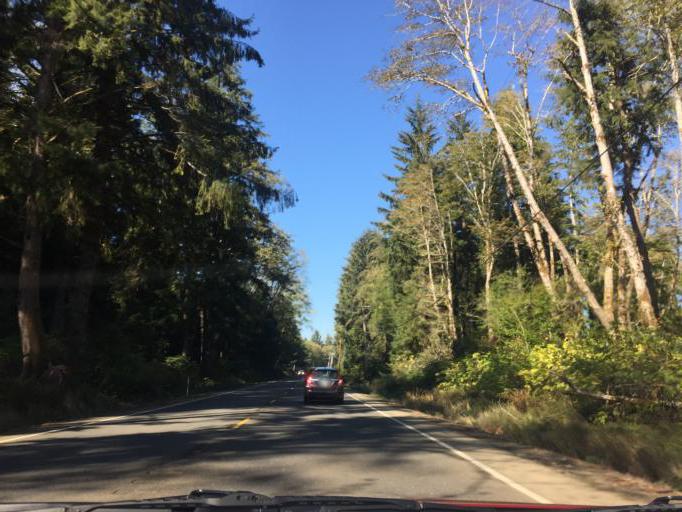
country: US
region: Oregon
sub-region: Clatsop County
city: Cannon Beach
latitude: 45.9044
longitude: -123.8756
